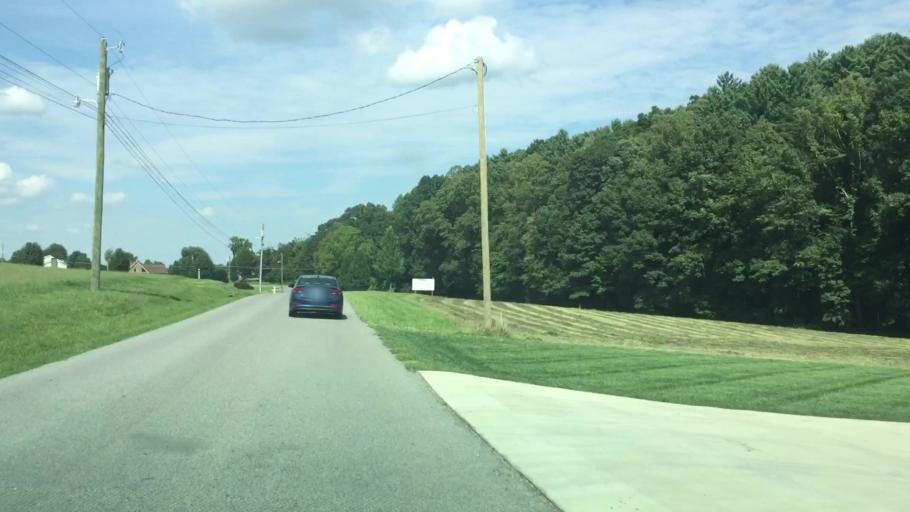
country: US
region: Tennessee
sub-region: Sullivan County
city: Fairmount
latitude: 36.5963
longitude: -82.0519
